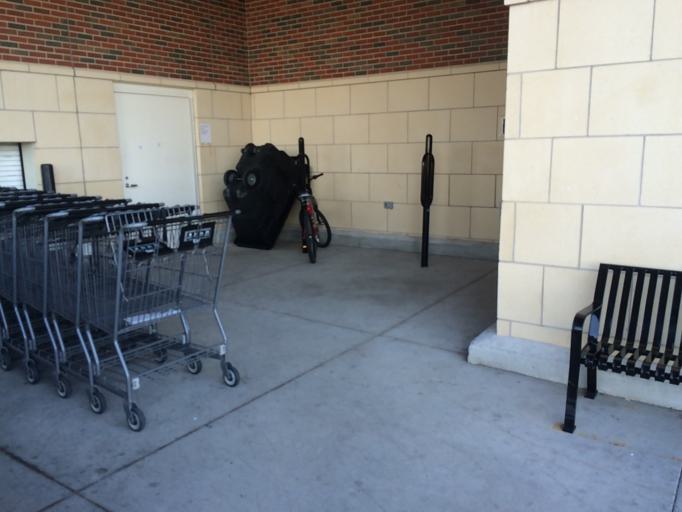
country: US
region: Oklahoma
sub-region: Cleveland County
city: Norman
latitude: 35.2374
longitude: -97.4794
